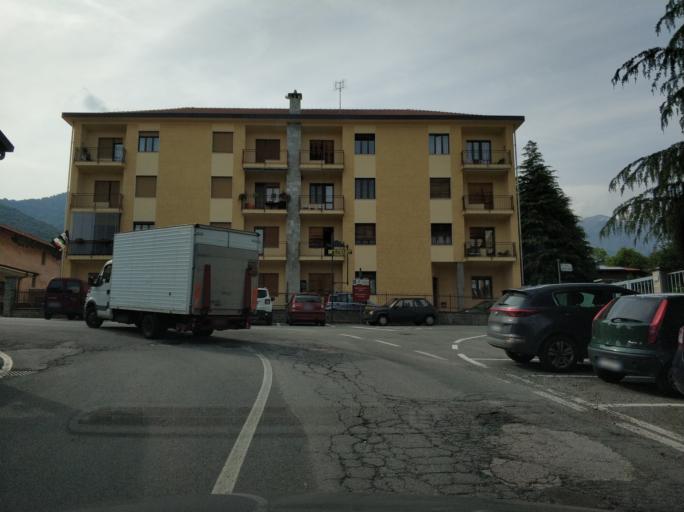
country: IT
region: Piedmont
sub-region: Provincia di Torino
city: Corio
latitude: 45.3140
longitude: 7.5317
